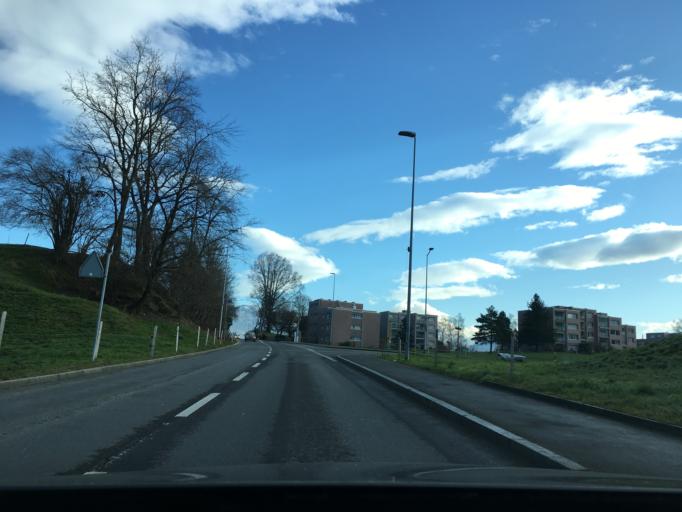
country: CH
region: Lucerne
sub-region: Lucerne-Land District
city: Adligenswil
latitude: 47.0516
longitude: 8.3521
